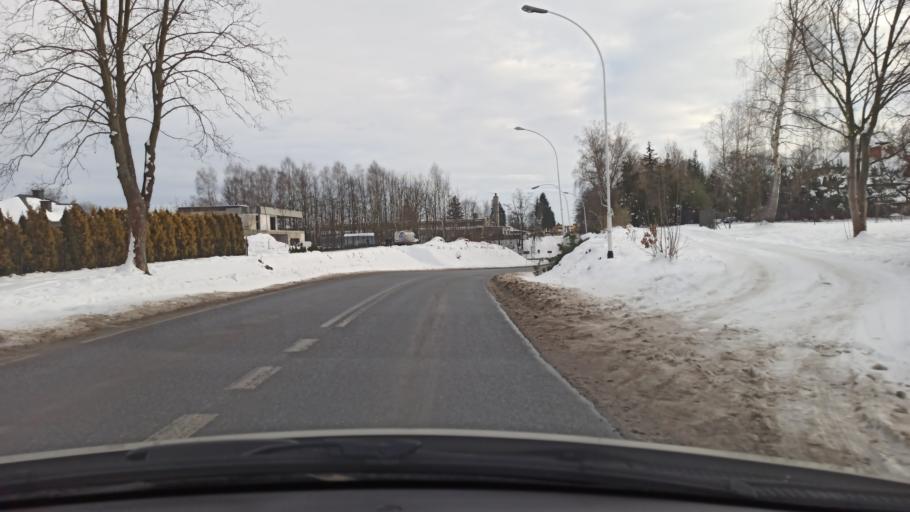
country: PL
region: Subcarpathian Voivodeship
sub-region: Powiat lezajski
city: Lezajsk
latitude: 50.2503
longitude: 22.4298
